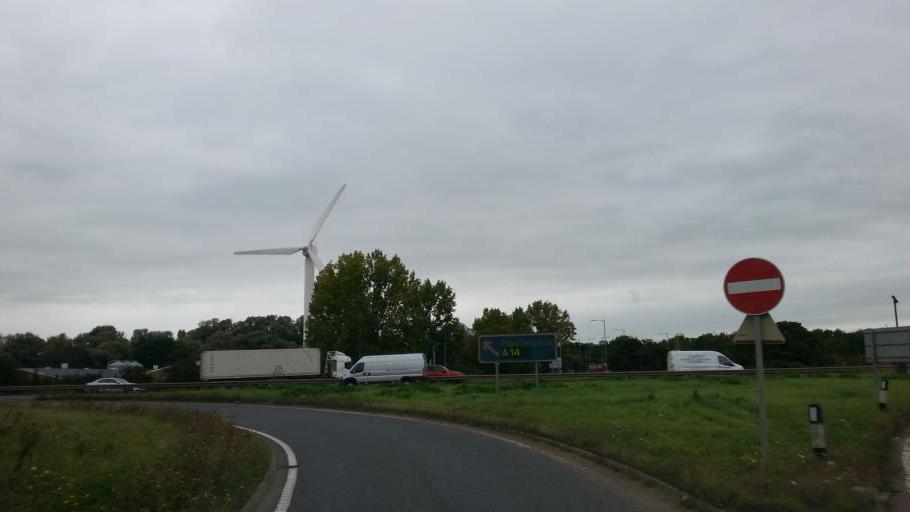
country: GB
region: England
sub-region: Cambridgeshire
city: Hemingford Grey
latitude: 52.3024
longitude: -0.0924
